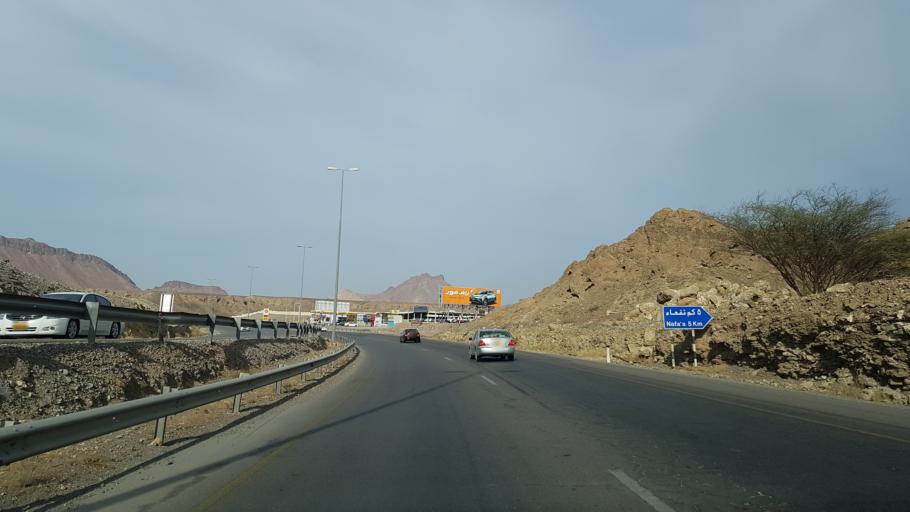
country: OM
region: Muhafazat ad Dakhiliyah
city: Bidbid
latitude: 23.4161
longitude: 58.1154
